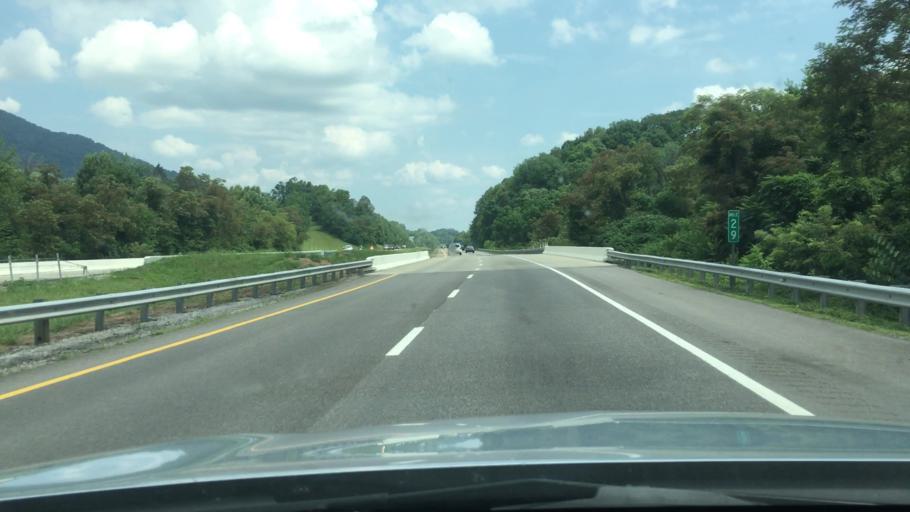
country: US
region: Tennessee
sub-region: Unicoi County
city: Unicoi
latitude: 36.2408
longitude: -82.3271
